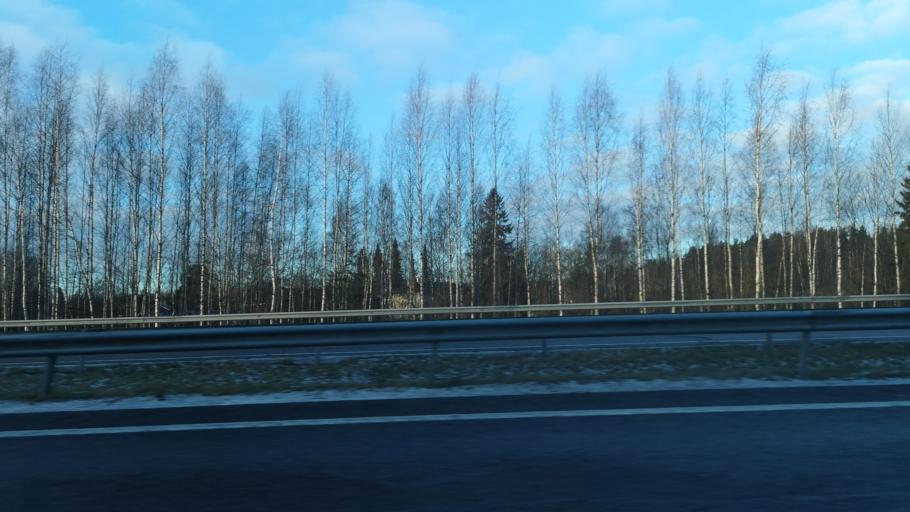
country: FI
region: Paijanne Tavastia
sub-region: Lahti
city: Heinola
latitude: 61.3003
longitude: 26.0850
